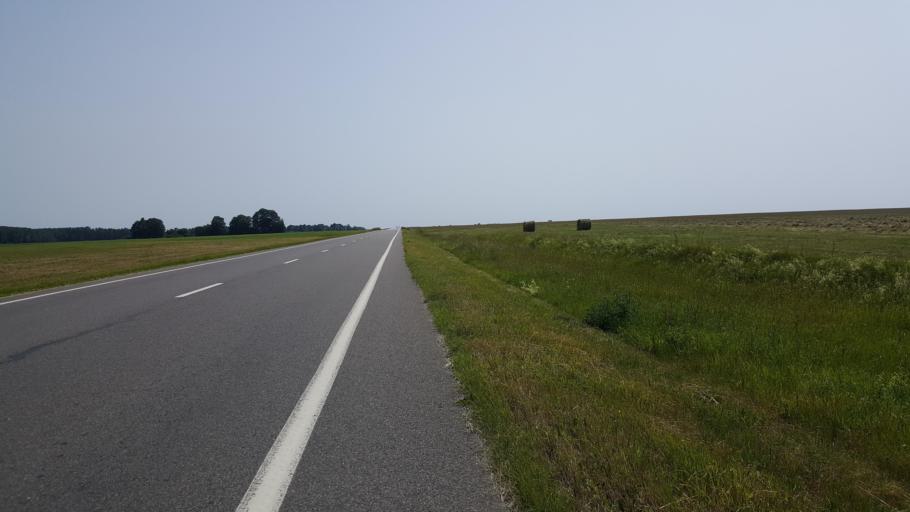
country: BY
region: Brest
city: Kamyanyets
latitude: 52.4504
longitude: 23.8337
